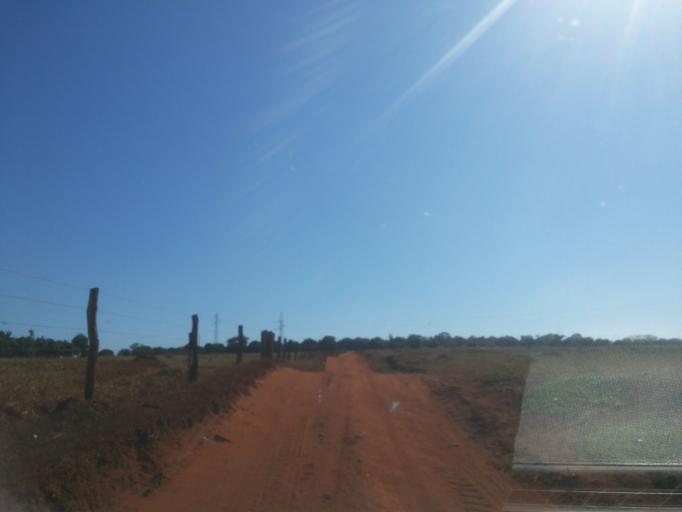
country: BR
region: Minas Gerais
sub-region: Centralina
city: Centralina
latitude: -18.7294
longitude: -49.1783
